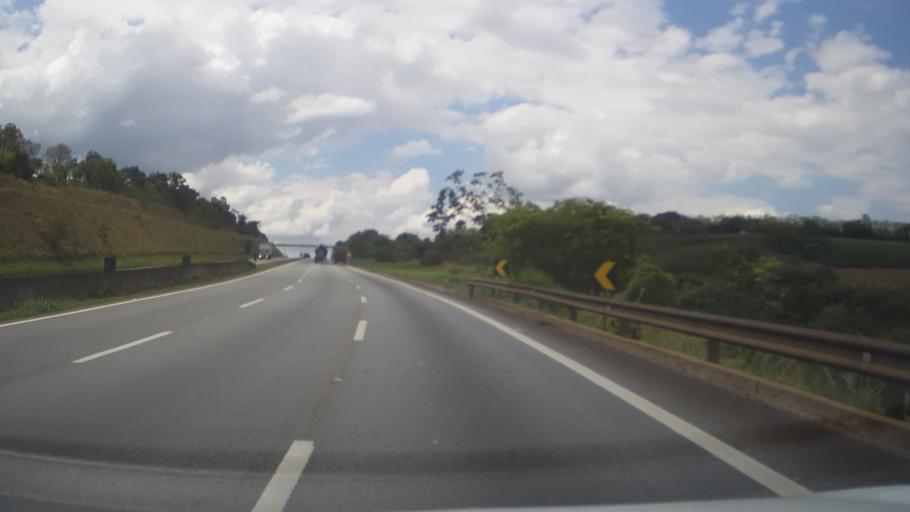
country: BR
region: Minas Gerais
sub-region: Nepomuceno
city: Nepomuceno
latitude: -21.2845
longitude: -45.1400
